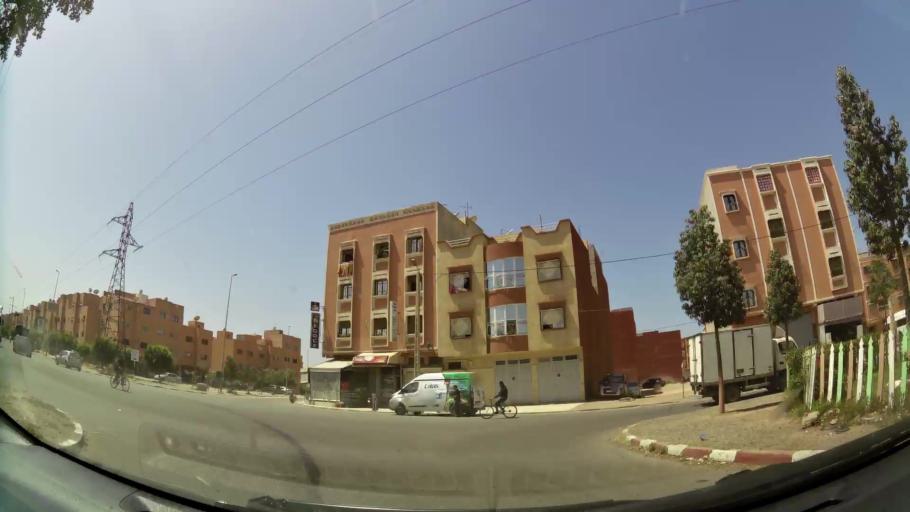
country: MA
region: Souss-Massa-Draa
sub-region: Inezgane-Ait Mellou
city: Inezgane
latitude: 30.3289
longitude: -9.4972
